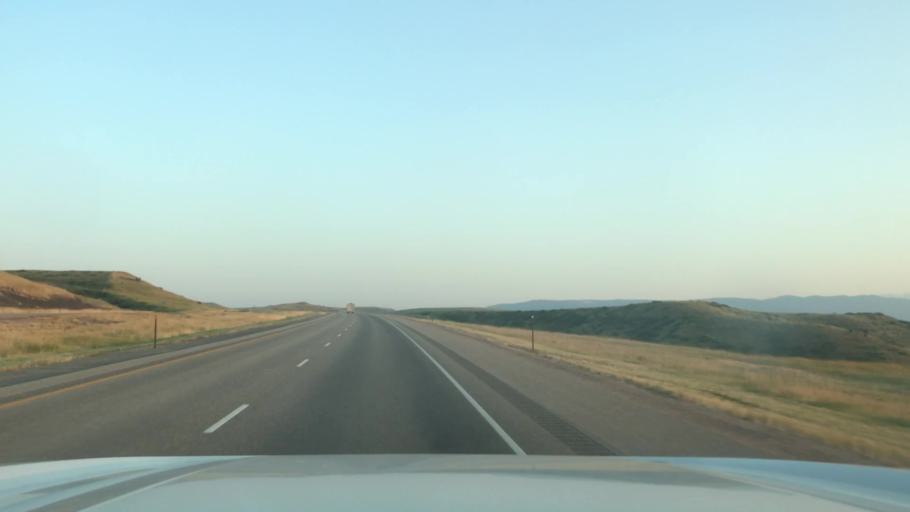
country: US
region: Wyoming
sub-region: Sheridan County
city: Sheridan
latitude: 44.7272
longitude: -106.9189
